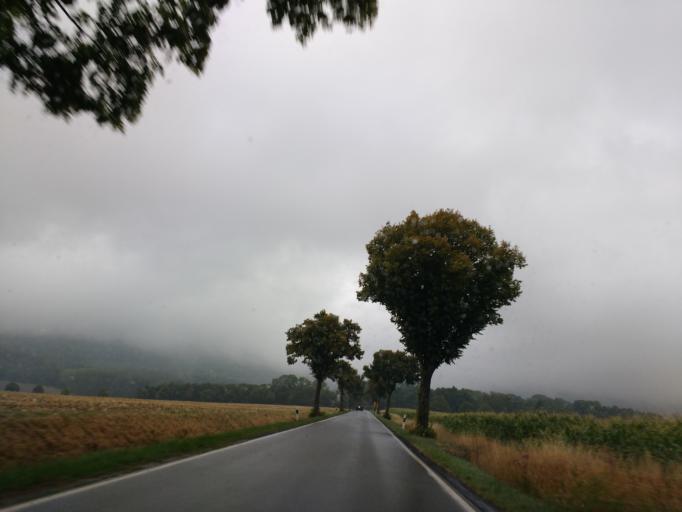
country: DE
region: Lower Saxony
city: Heyen
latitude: 52.0598
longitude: 9.5196
